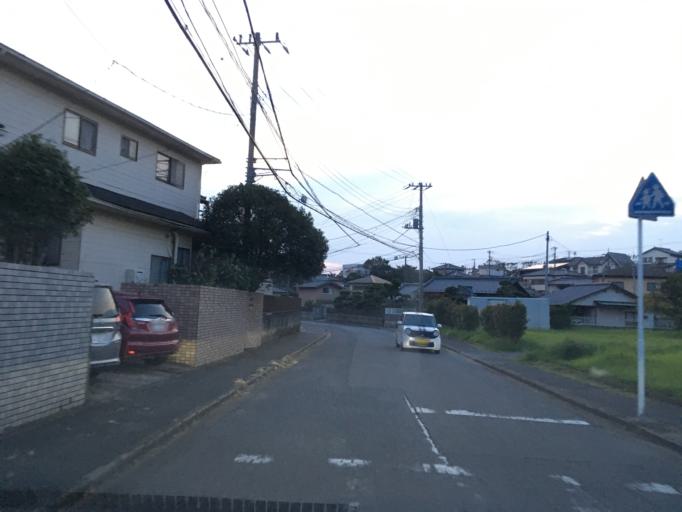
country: JP
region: Chiba
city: Kimitsu
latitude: 35.3448
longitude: 139.9099
